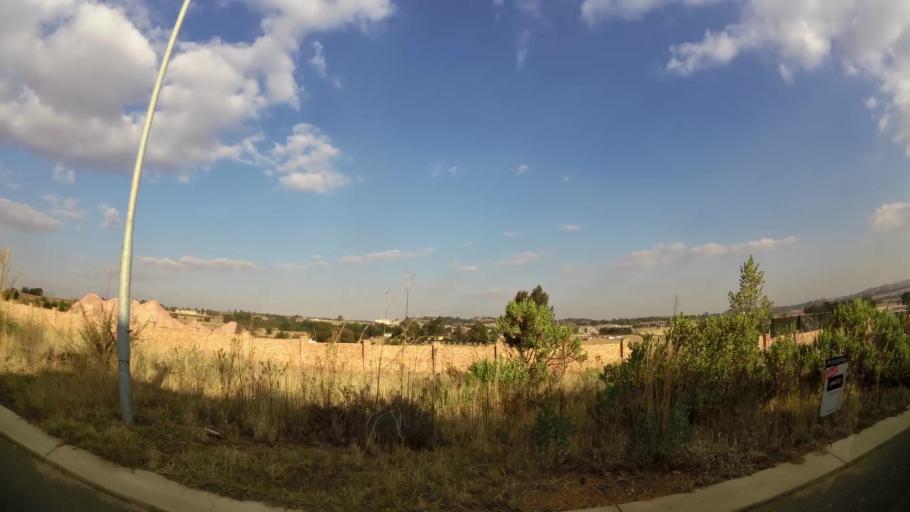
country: ZA
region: Gauteng
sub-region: West Rand District Municipality
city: Krugersdorp
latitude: -26.1040
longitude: 27.7317
